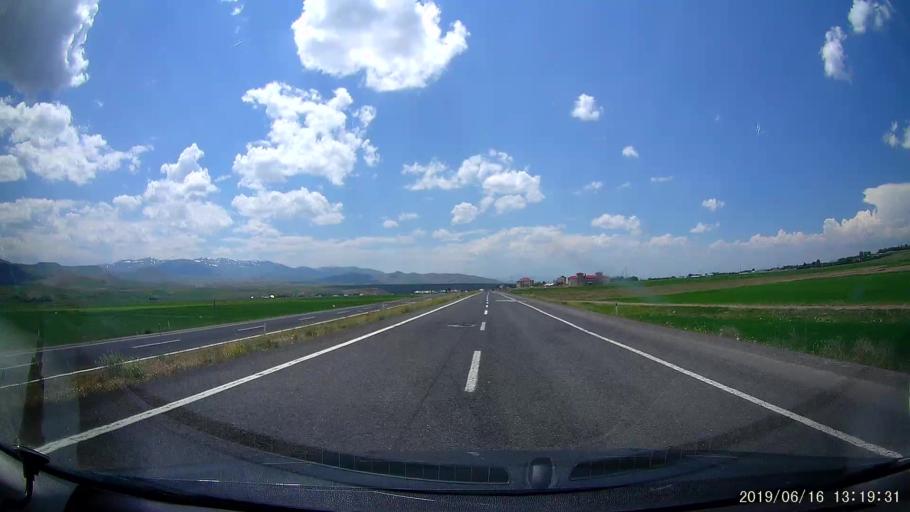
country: TR
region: Agri
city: Taslicay
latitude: 39.6328
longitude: 43.4050
